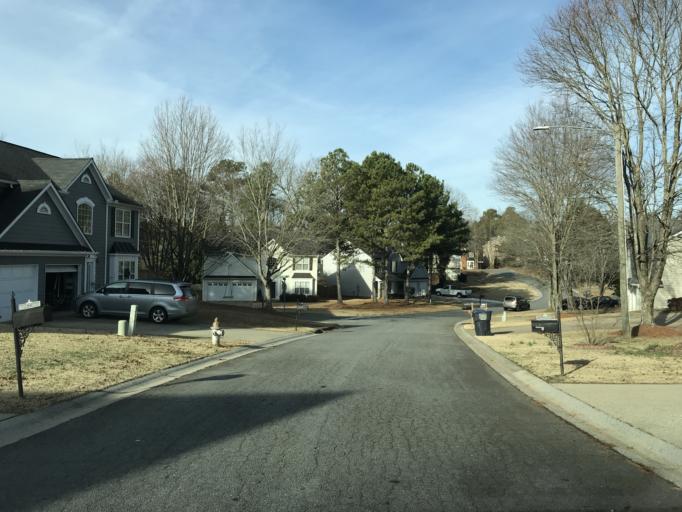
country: US
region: Georgia
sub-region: Cobb County
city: Kennesaw
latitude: 34.0583
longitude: -84.5950
